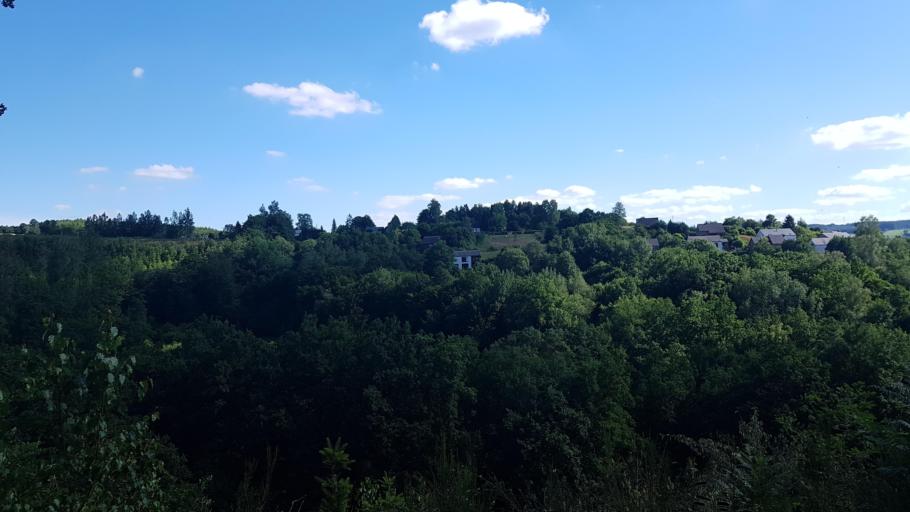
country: BE
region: Wallonia
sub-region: Province du Luxembourg
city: Bouillon
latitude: 49.8032
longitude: 5.0828
